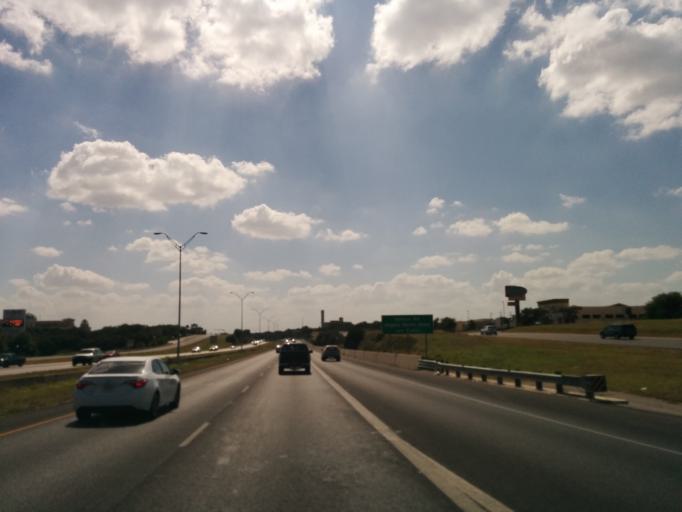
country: US
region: Texas
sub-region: Bexar County
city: Hollywood Park
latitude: 29.6087
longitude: -98.5158
